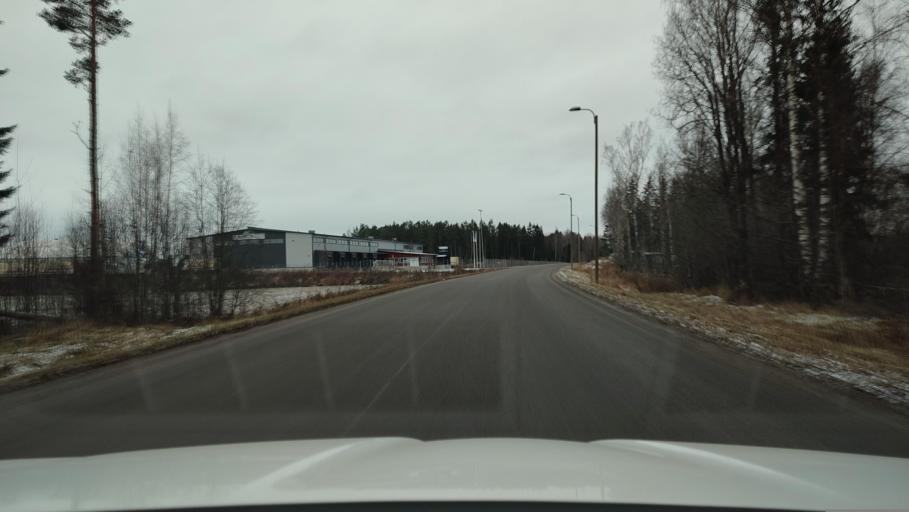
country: FI
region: Ostrobothnia
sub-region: Vaasa
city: Ristinummi
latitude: 63.0375
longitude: 21.7814
